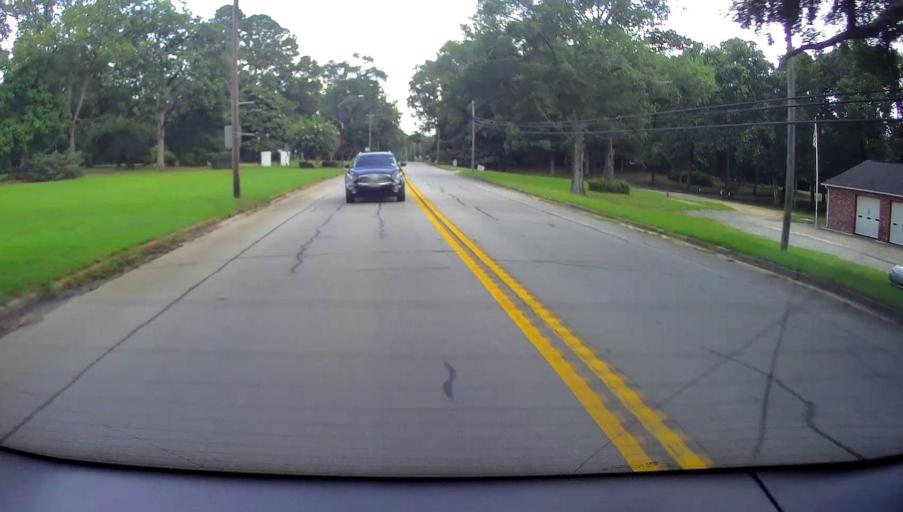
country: US
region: Georgia
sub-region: Meriwether County
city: Greenville
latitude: 33.0992
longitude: -84.5787
